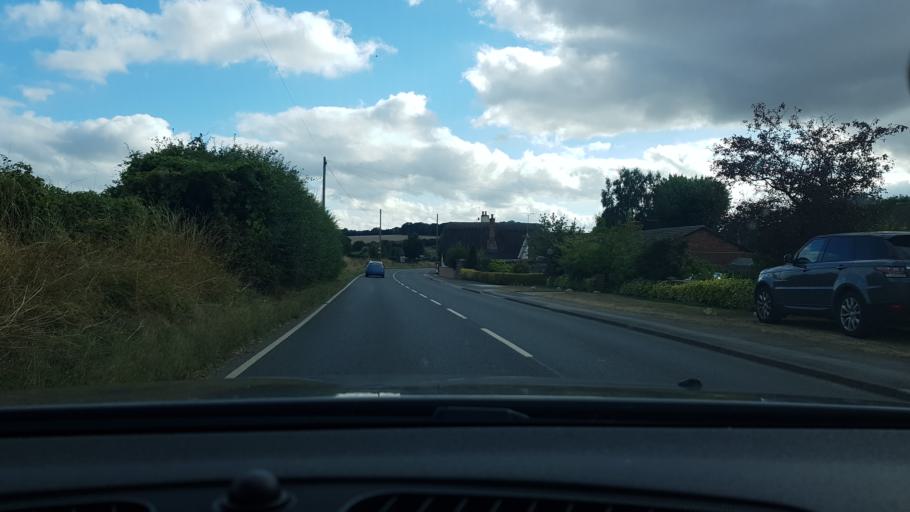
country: GB
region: England
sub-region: West Berkshire
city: Wickham
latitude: 51.4771
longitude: -1.4428
